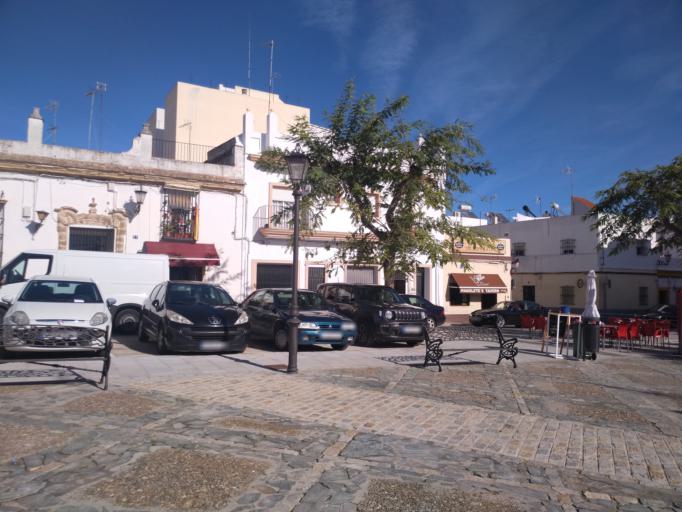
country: ES
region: Andalusia
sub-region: Provincia de Cadiz
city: San Fernando
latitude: 36.4689
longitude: -6.1919
